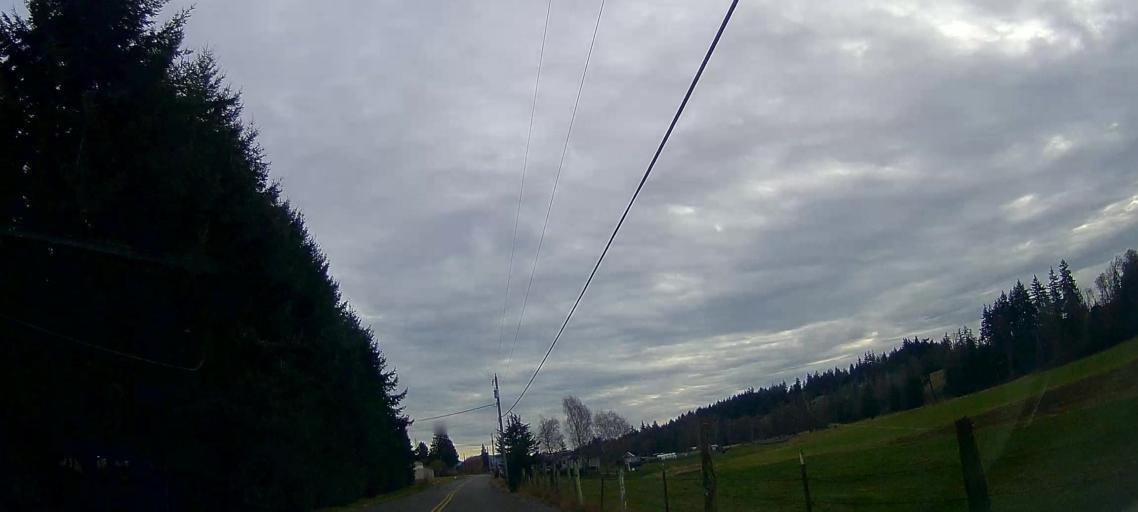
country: US
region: Washington
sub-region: Skagit County
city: Burlington
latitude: 48.5113
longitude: -122.4277
